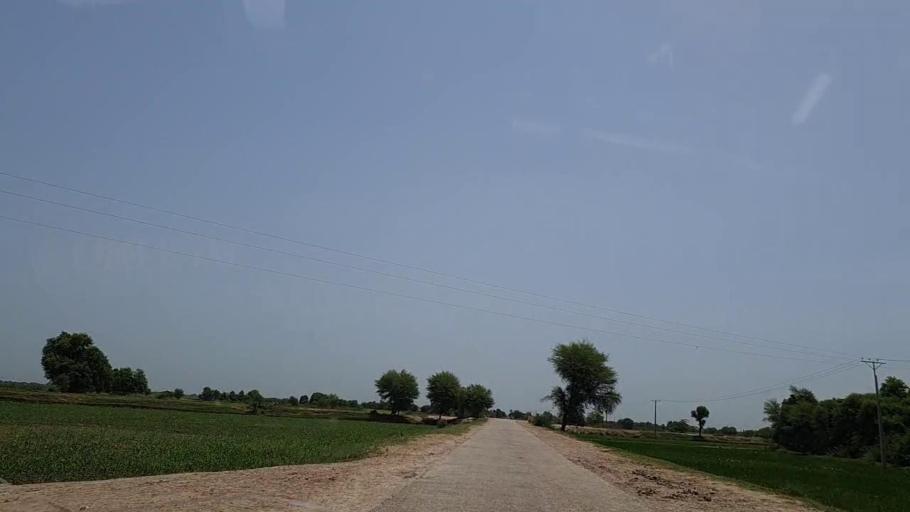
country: PK
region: Sindh
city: Tharu Shah
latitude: 26.9572
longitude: 68.0736
